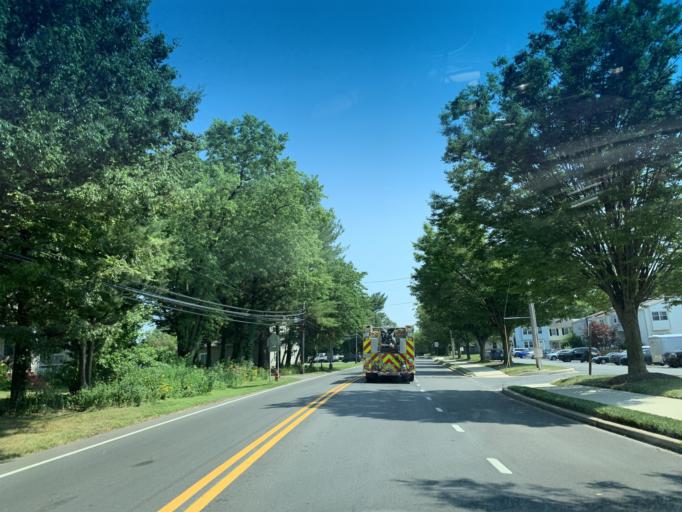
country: US
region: Maryland
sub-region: Montgomery County
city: Poolesville
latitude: 39.1421
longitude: -77.4074
